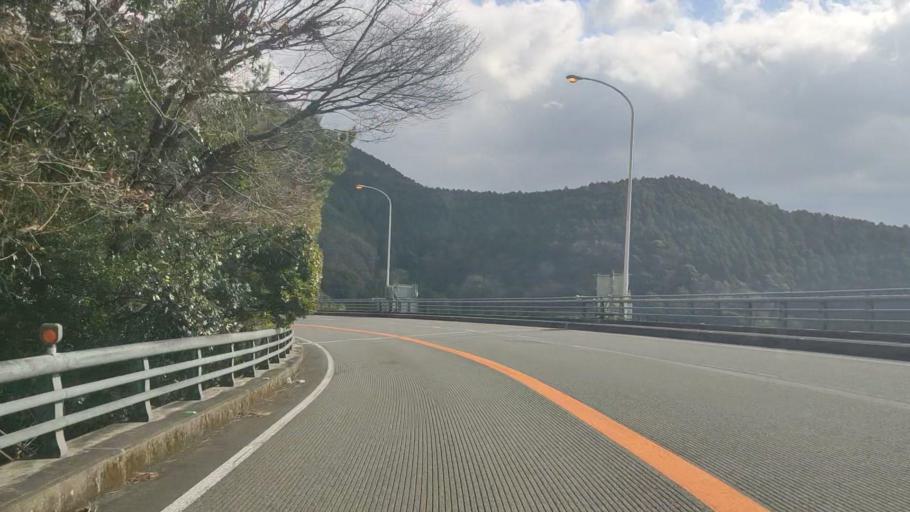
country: JP
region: Kumamoto
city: Hitoyoshi
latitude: 32.0790
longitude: 130.7989
